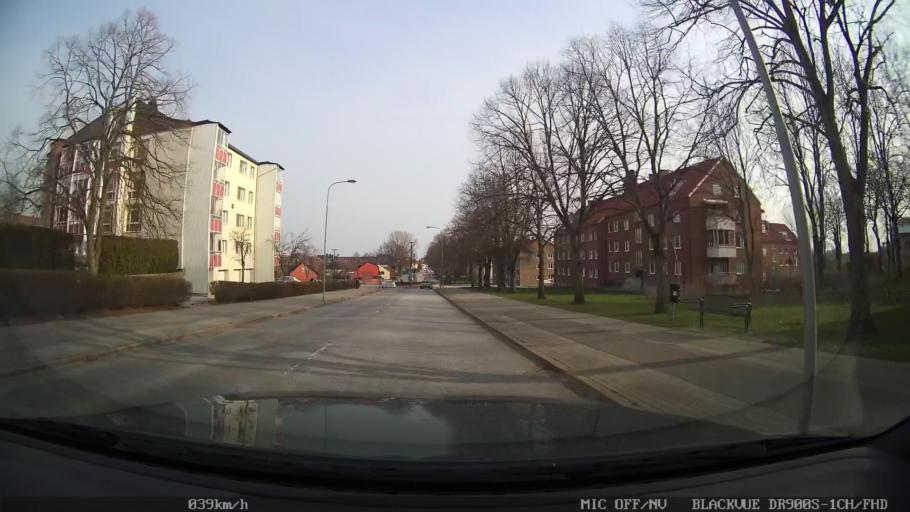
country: SE
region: Skane
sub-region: Ystads Kommun
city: Ystad
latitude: 55.4353
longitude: 13.8123
